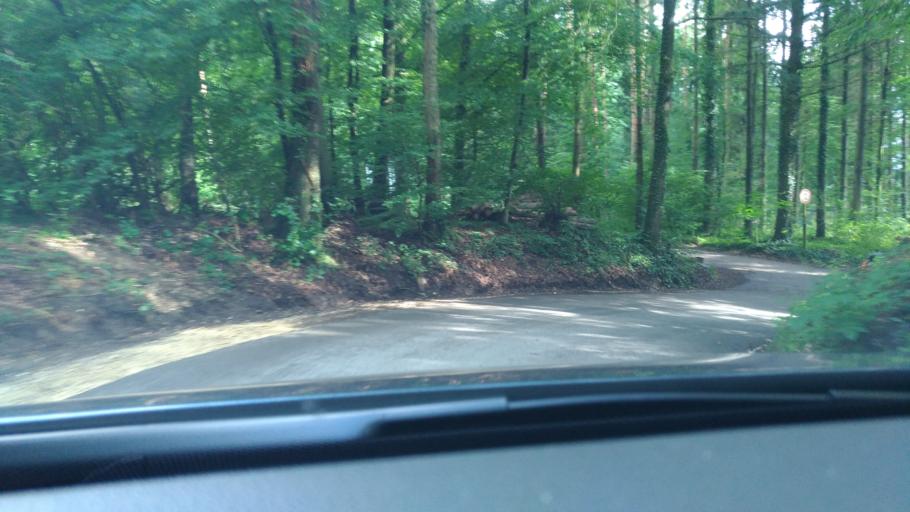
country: DE
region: Baden-Wuerttemberg
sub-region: Tuebingen Region
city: Sipplingen
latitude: 47.7913
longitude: 9.1235
